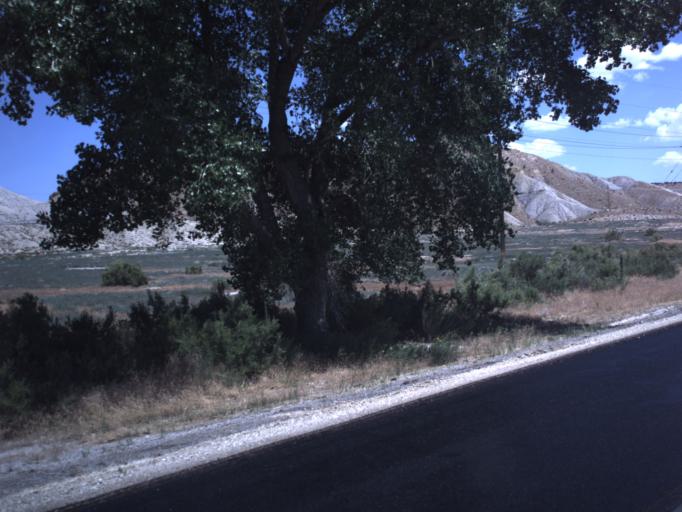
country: US
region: Utah
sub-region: Emery County
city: Orangeville
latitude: 39.2577
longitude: -111.1031
